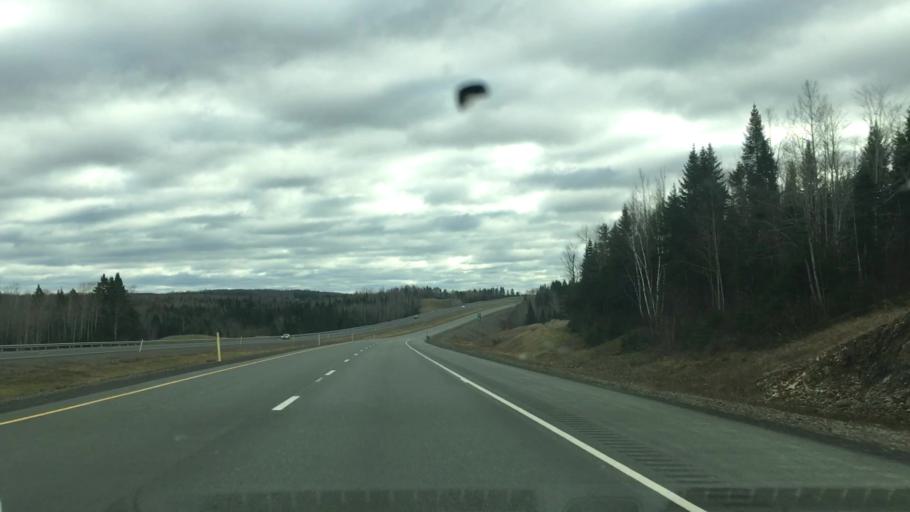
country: CA
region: New Brunswick
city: Florenceville-Bristol
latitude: 46.5425
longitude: -67.7165
